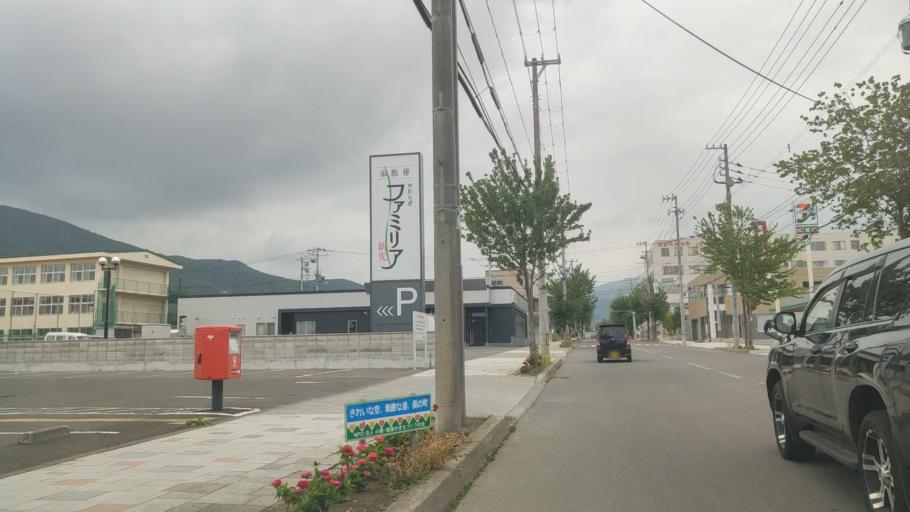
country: JP
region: Hokkaido
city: Otaru
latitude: 43.1744
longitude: 141.0564
